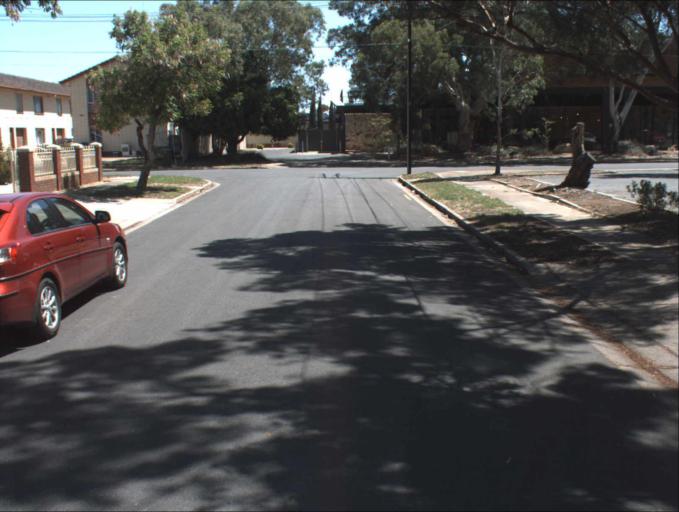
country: AU
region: South Australia
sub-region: Charles Sturt
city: Woodville North
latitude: -34.8512
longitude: 138.5532
